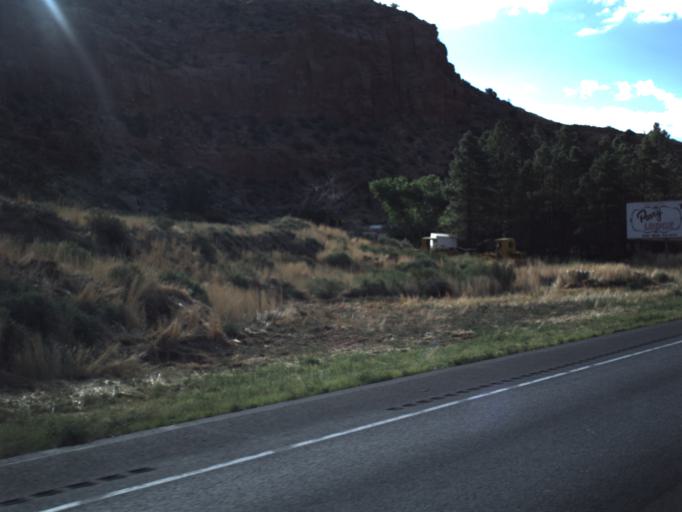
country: US
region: Utah
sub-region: Kane County
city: Kanab
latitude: 37.0575
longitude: -112.5364
